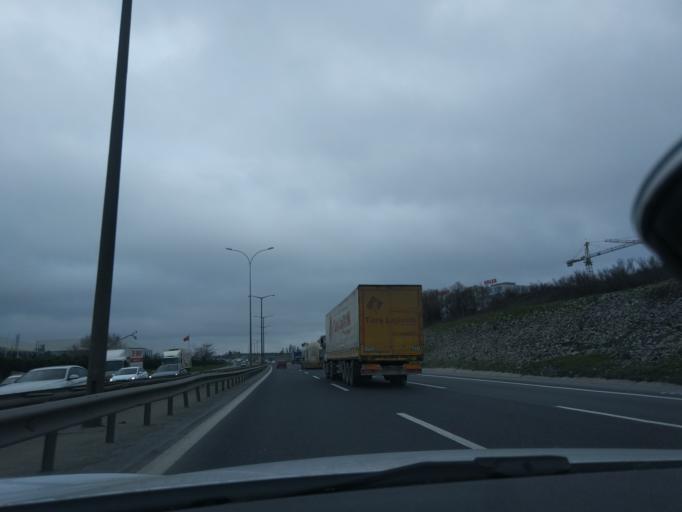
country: TR
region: Istanbul
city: Esenyurt
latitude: 41.0699
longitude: 28.6495
